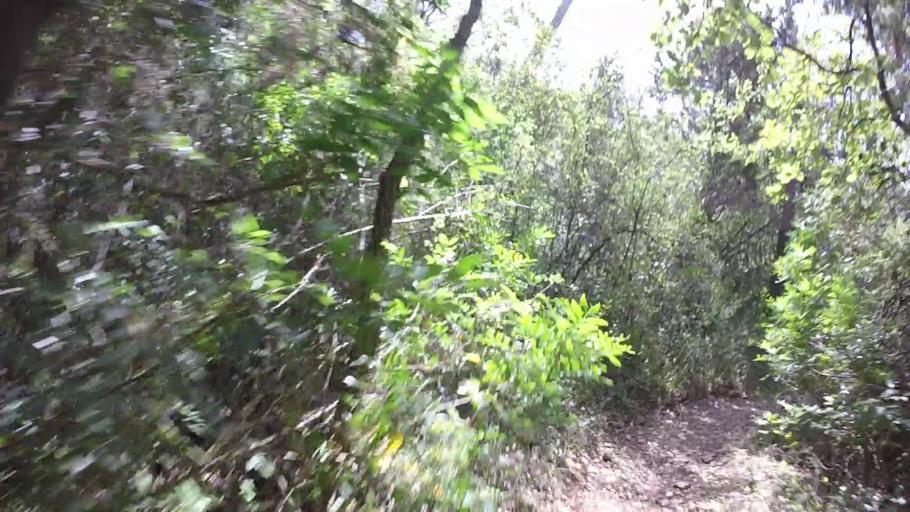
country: FR
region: Provence-Alpes-Cote d'Azur
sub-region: Departement des Alpes-Maritimes
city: Mougins
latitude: 43.6153
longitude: 7.0222
